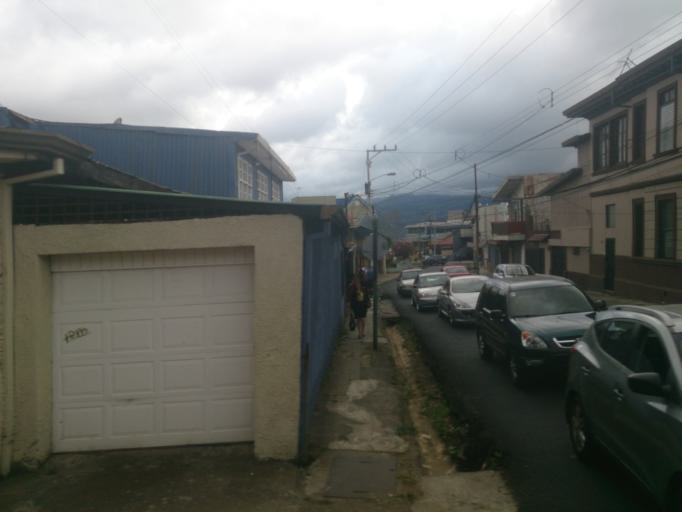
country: CR
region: San Jose
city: Calle Blancos
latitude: 9.9340
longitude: -84.0671
